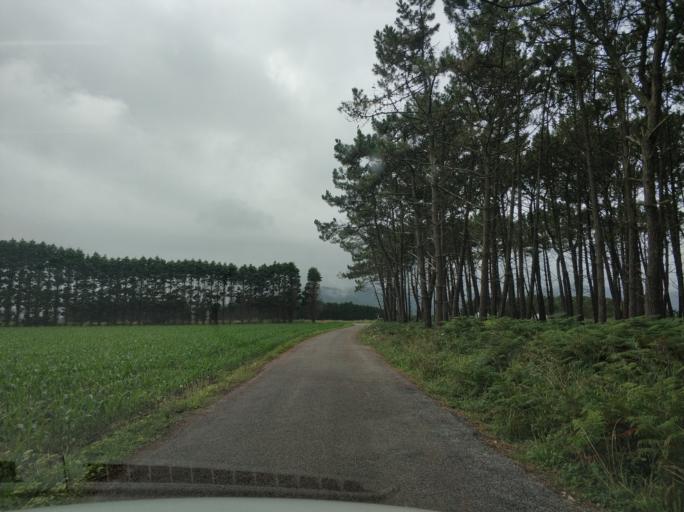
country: ES
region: Asturias
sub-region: Province of Asturias
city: Tineo
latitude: 43.5657
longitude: -6.4702
